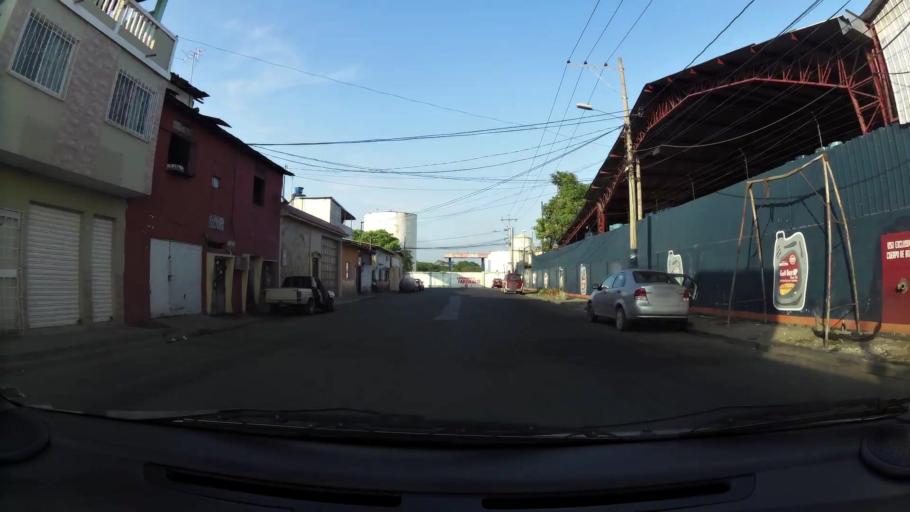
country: EC
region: Guayas
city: Eloy Alfaro
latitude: -2.1730
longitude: -79.8542
